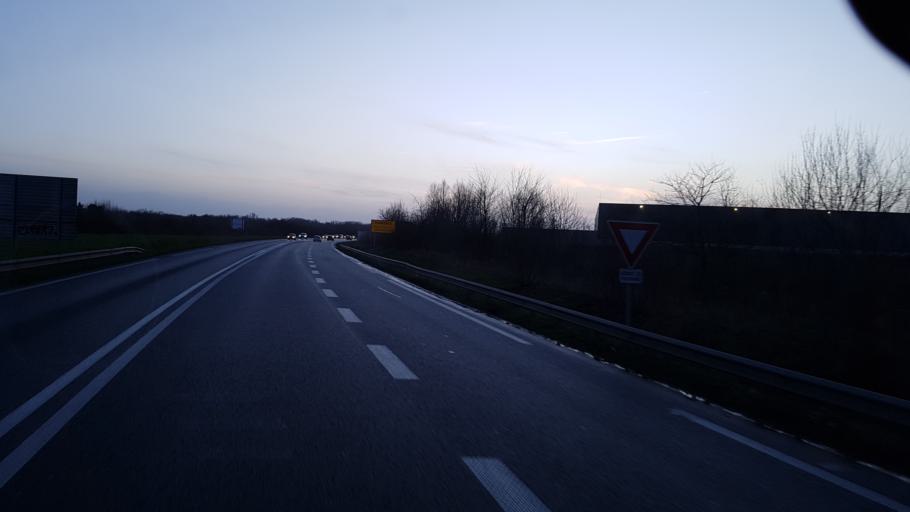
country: FR
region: Nord-Pas-de-Calais
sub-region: Departement du Nord
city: Lauwin-Planque
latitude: 50.3964
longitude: 3.0399
